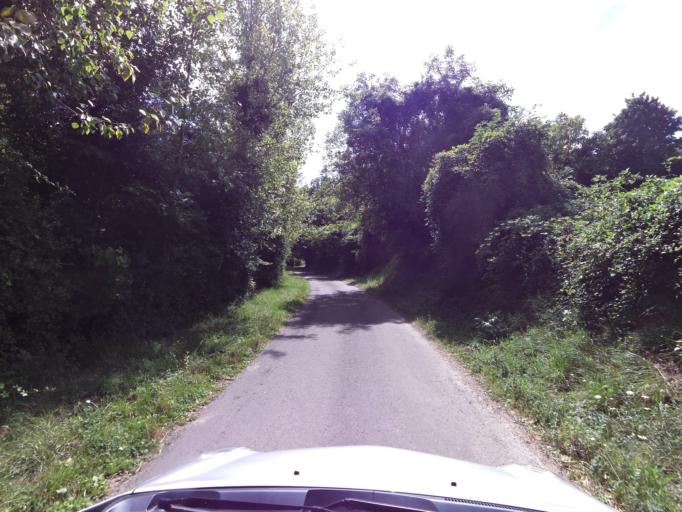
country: FR
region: Picardie
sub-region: Departement de l'Aisne
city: Bruyeres-et-Montberault
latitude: 49.4808
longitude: 3.6423
